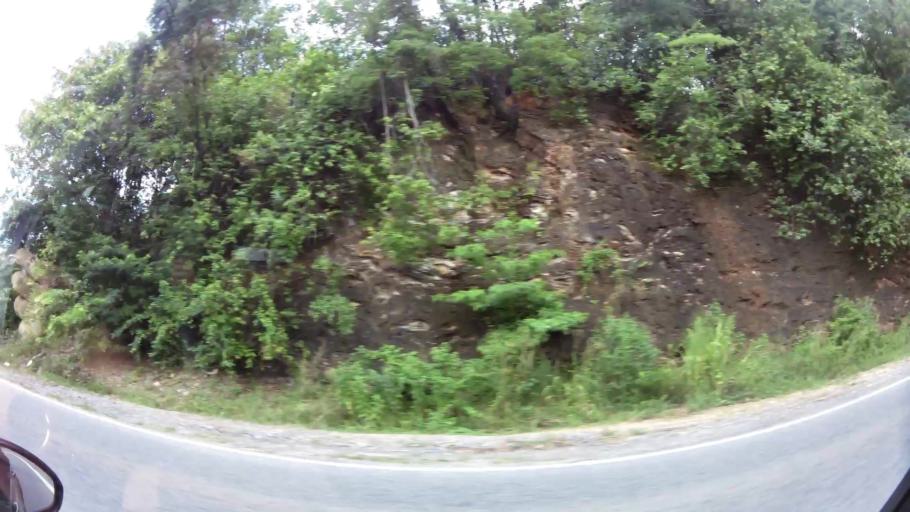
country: TT
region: City of Port of Spain
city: Port-of-Spain
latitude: 10.6738
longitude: -61.5038
